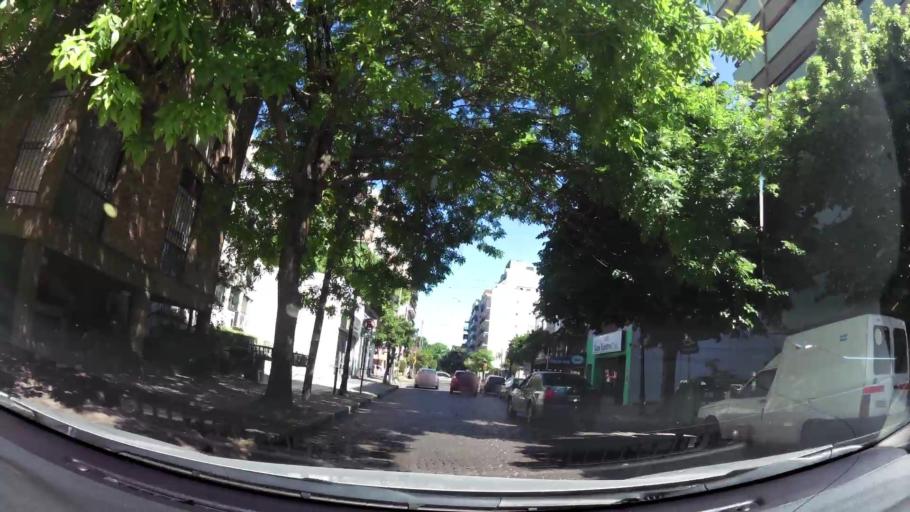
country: AR
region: Buenos Aires
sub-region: Partido de San Isidro
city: San Isidro
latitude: -34.4704
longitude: -58.5083
